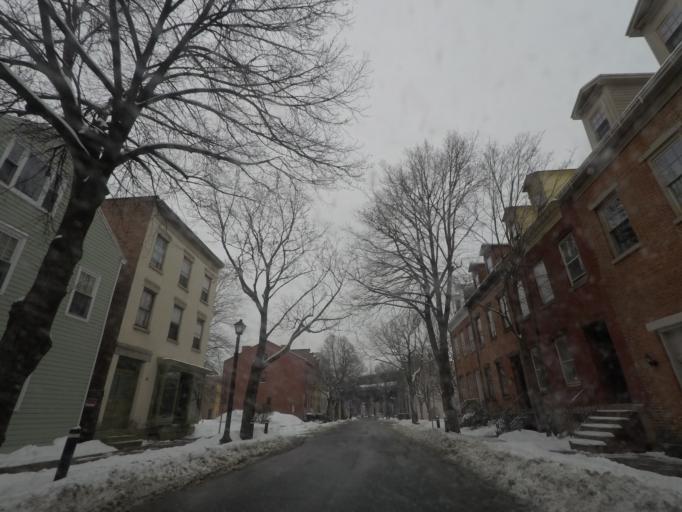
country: US
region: New York
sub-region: Albany County
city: Albany
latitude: 42.6435
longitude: -73.7535
